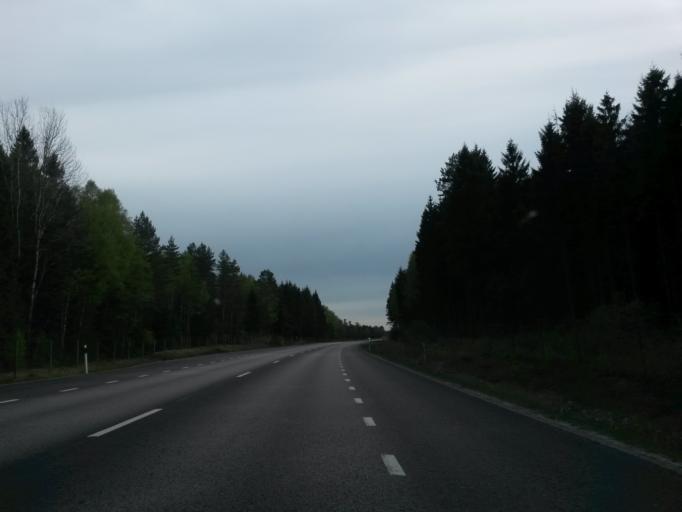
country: SE
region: Vaestra Goetaland
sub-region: Vara Kommun
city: Vara
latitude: 58.1832
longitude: 12.8967
